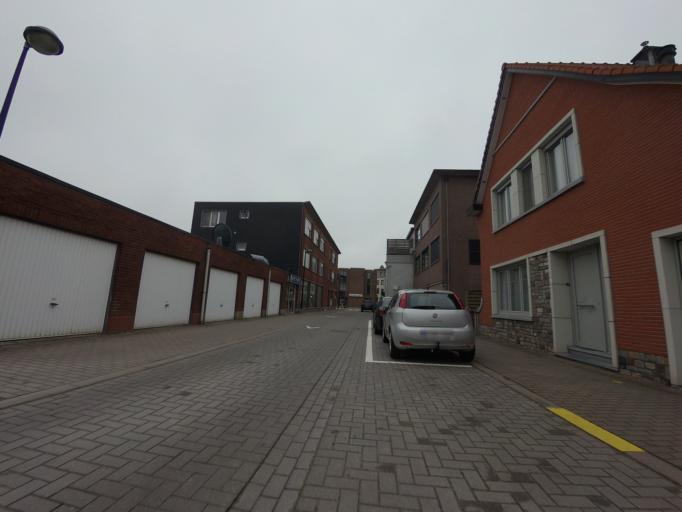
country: BE
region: Flanders
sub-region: Provincie Vlaams-Brabant
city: Kortenberg
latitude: 50.8876
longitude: 4.5390
